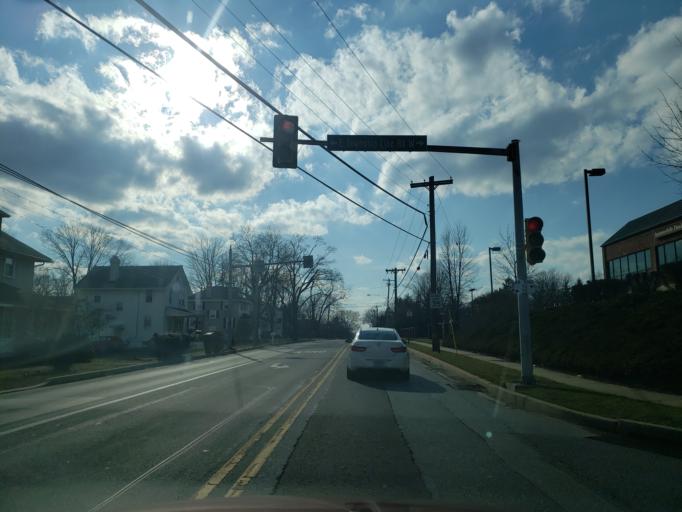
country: US
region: Pennsylvania
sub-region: Montgomery County
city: Norristown
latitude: 40.1499
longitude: -75.3102
